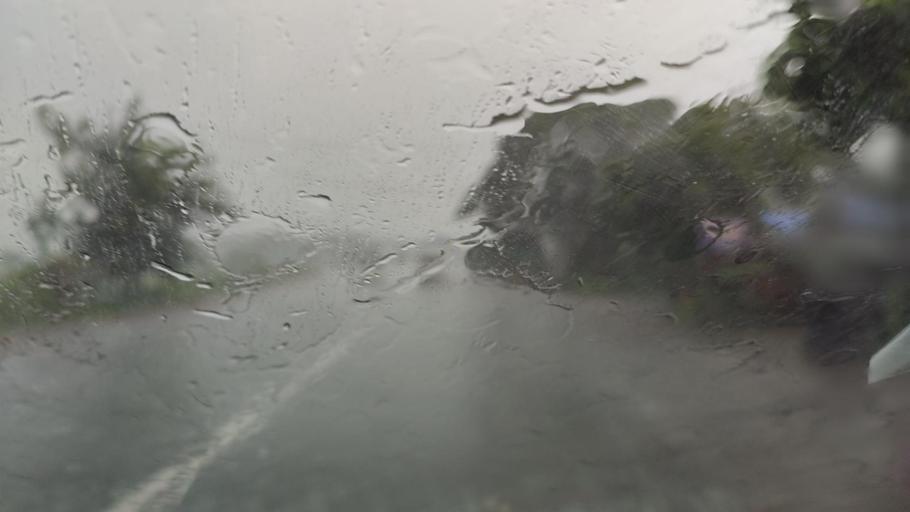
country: MM
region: Bago
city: Bago
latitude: 17.5696
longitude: 96.5487
